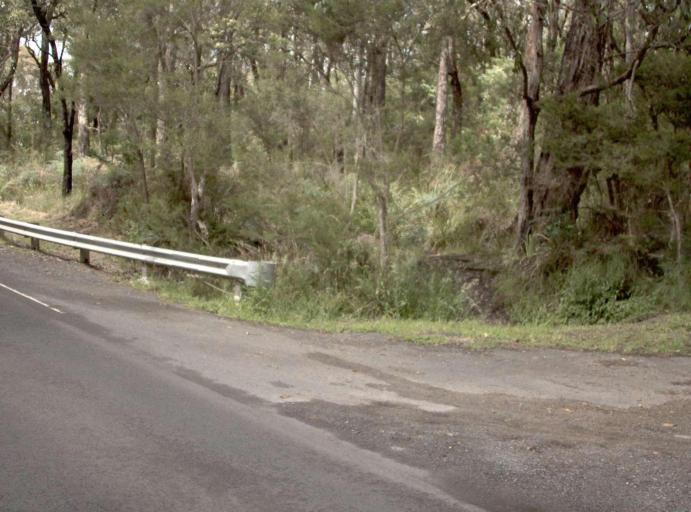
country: AU
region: Victoria
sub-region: Mornington Peninsula
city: Dromana
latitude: -38.3597
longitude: 144.9685
